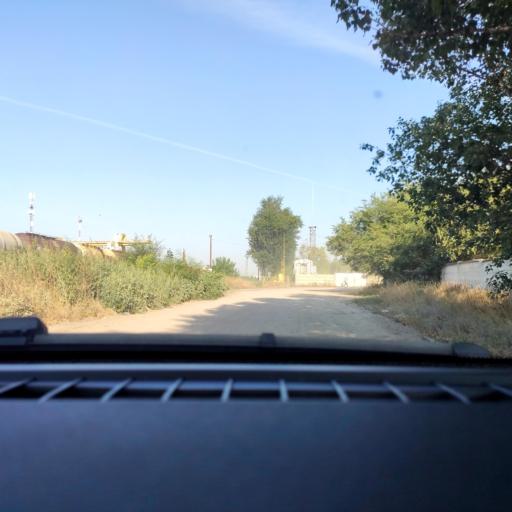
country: RU
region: Voronezj
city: Voronezh
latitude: 51.6454
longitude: 39.2769
